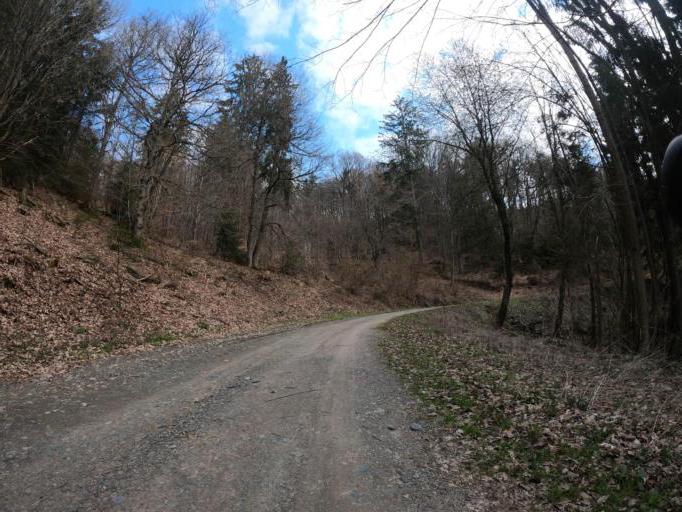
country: DE
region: North Rhine-Westphalia
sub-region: Regierungsbezirk Koln
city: Simmerath
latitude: 50.5924
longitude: 6.3377
